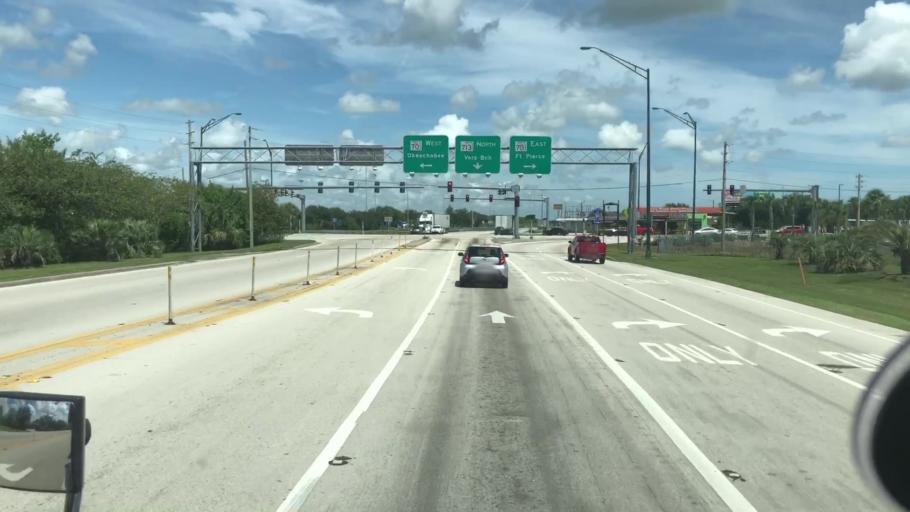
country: US
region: Florida
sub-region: Saint Lucie County
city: Fort Pierce South
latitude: 27.4116
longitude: -80.3988
